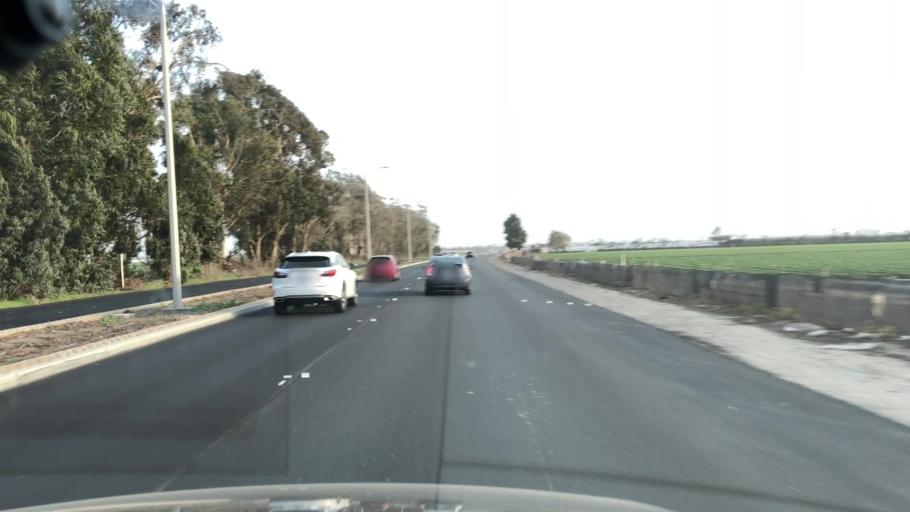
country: US
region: California
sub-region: Ventura County
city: Oxnard Shores
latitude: 34.2154
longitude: -119.2212
